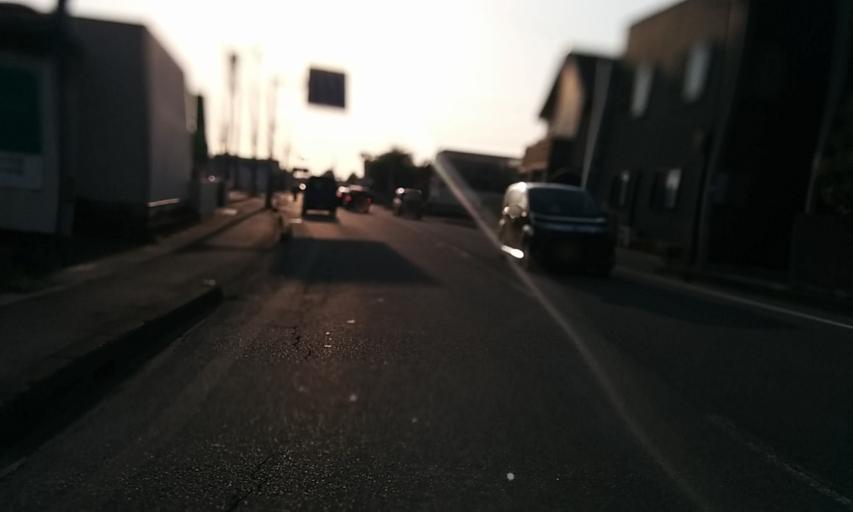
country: JP
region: Ehime
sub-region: Shikoku-chuo Shi
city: Matsuyama
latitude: 33.7813
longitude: 132.8154
